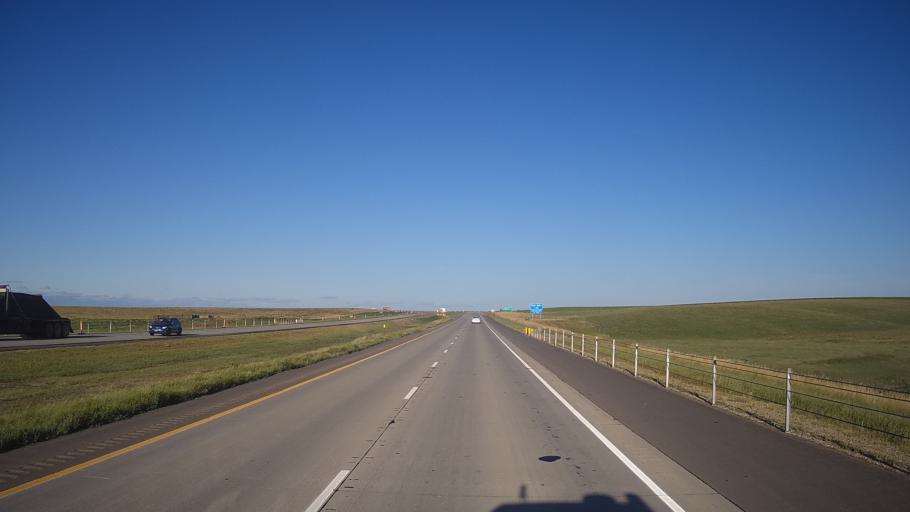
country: US
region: South Dakota
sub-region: Jackson County
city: Kadoka
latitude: 43.8426
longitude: -101.2585
